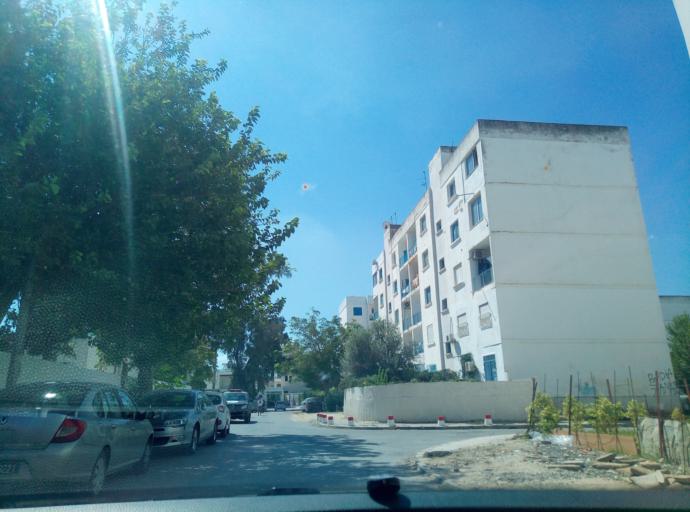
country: TN
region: Tunis
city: La Goulette
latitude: 36.8513
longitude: 10.2613
